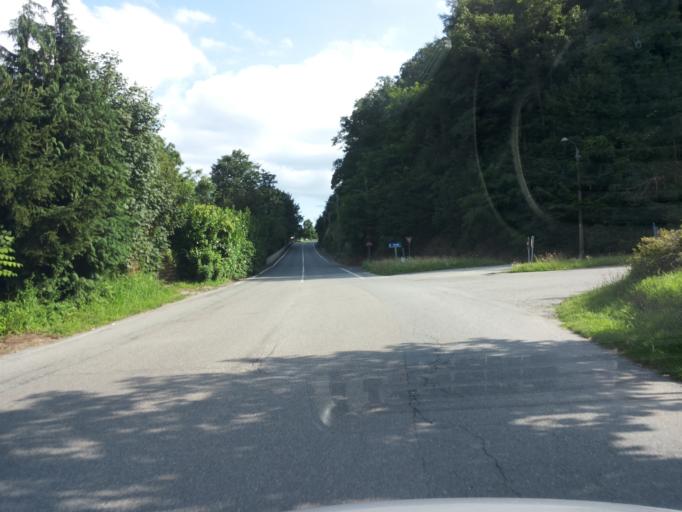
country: IT
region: Piedmont
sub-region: Provincia di Biella
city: Tollegno
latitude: 45.5979
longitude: 8.0533
